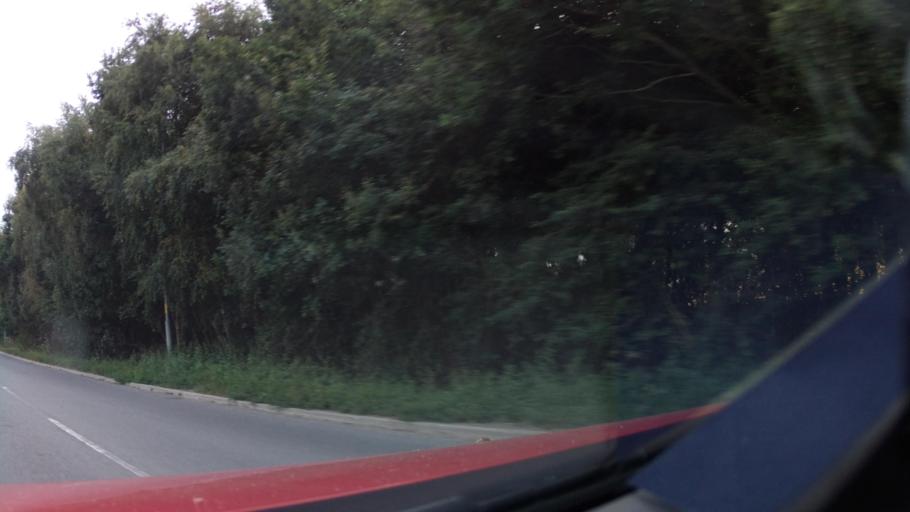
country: GB
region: England
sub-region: Lincolnshire
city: Skellingthorpe
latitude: 53.1523
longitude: -0.6706
